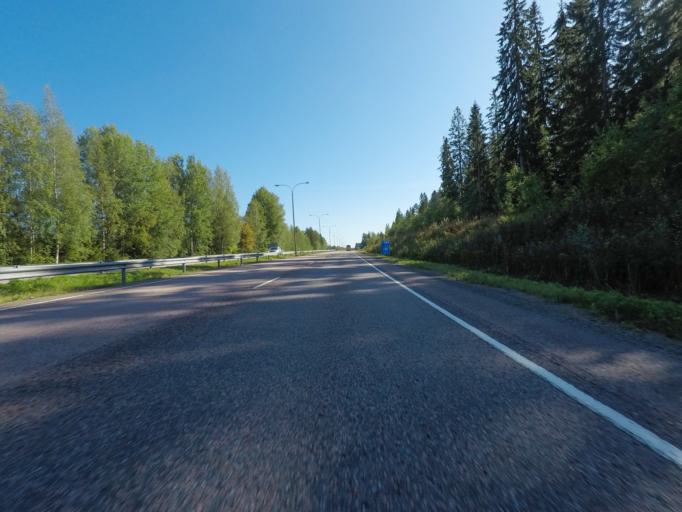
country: FI
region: Northern Savo
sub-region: Varkaus
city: Varkaus
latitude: 62.3122
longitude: 27.8539
